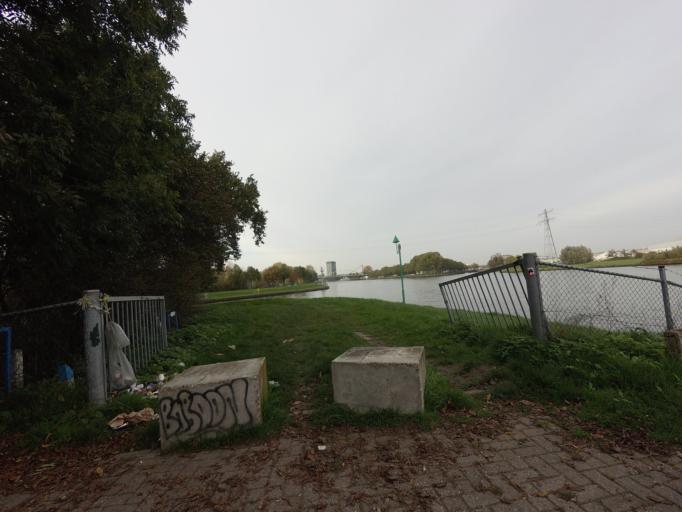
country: NL
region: Utrecht
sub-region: Gemeente Nieuwegein
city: Nieuwegein
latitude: 52.0473
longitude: 5.1057
